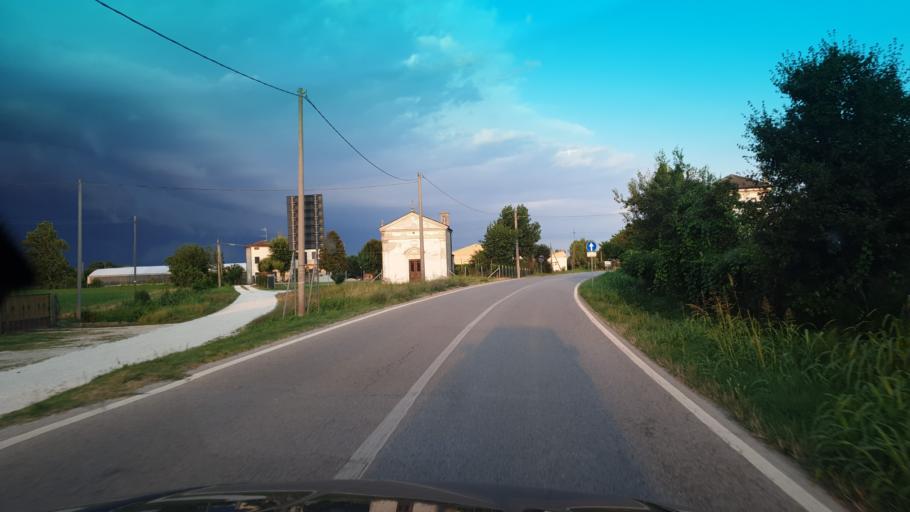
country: IT
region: Veneto
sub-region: Provincia di Rovigo
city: Lendinara
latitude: 45.0739
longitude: 11.6148
